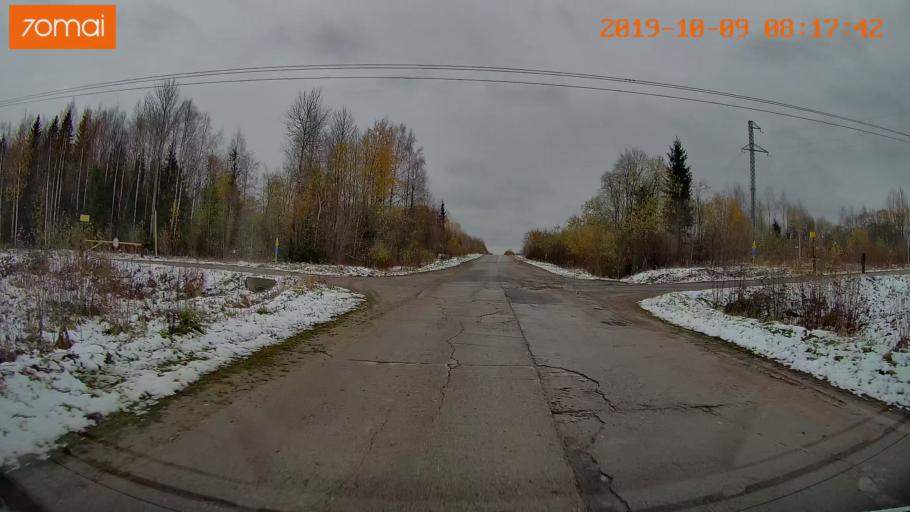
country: RU
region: Vologda
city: Gryazovets
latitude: 58.7391
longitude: 40.2102
